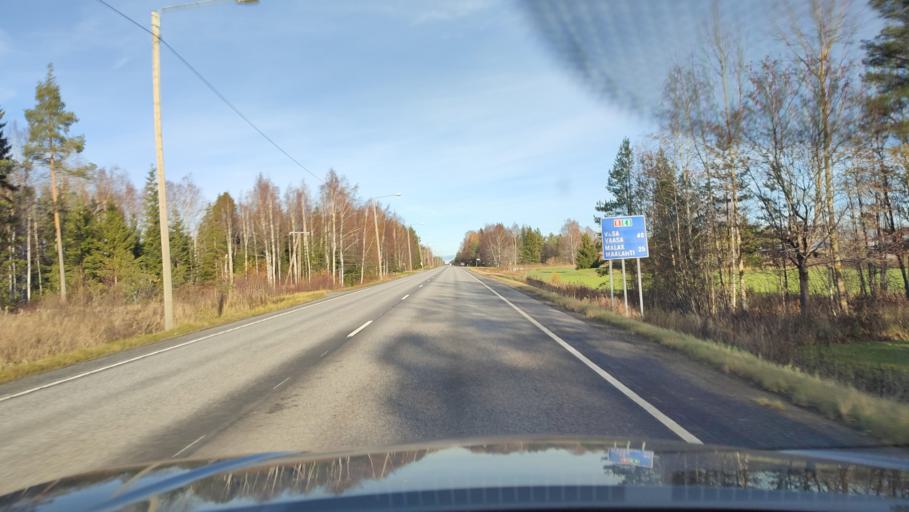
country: FI
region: Ostrobothnia
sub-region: Vaasa
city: Malax
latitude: 62.7759
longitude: 21.6611
